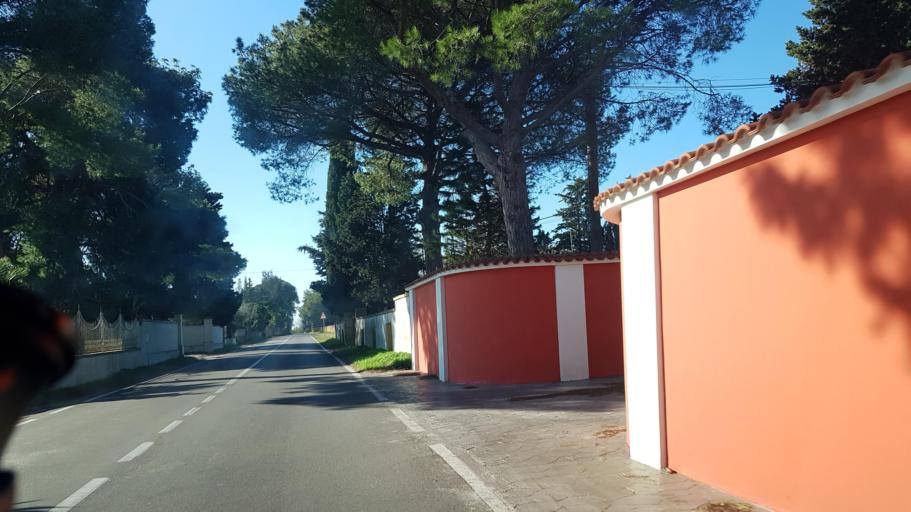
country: IT
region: Apulia
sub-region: Provincia di Lecce
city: Squinzano
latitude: 40.4253
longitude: 18.0315
